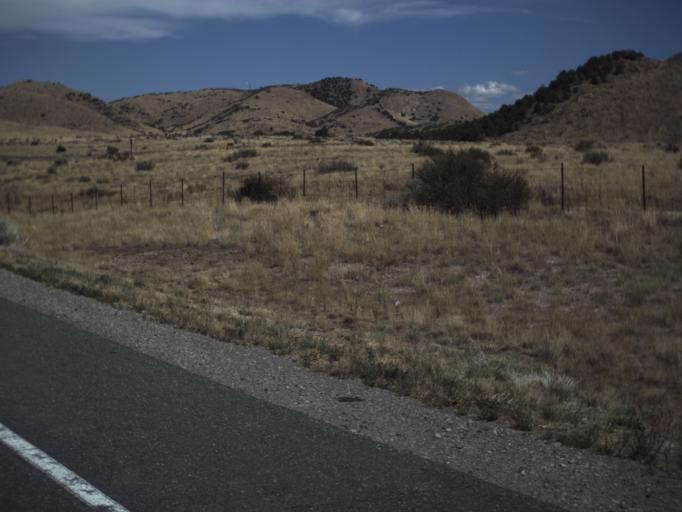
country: US
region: Utah
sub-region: Beaver County
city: Beaver
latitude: 38.6143
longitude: -112.6086
